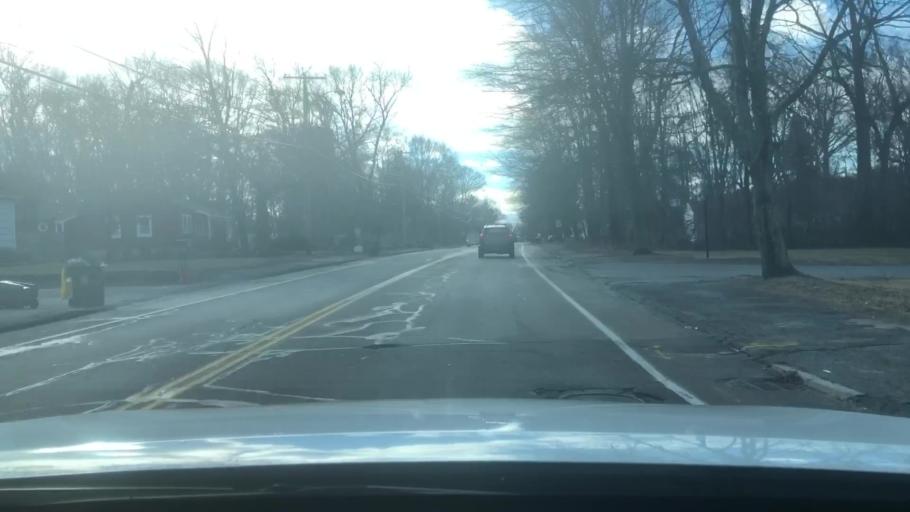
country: US
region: Massachusetts
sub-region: Norfolk County
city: Bellingham
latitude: 42.0830
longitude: -71.4738
